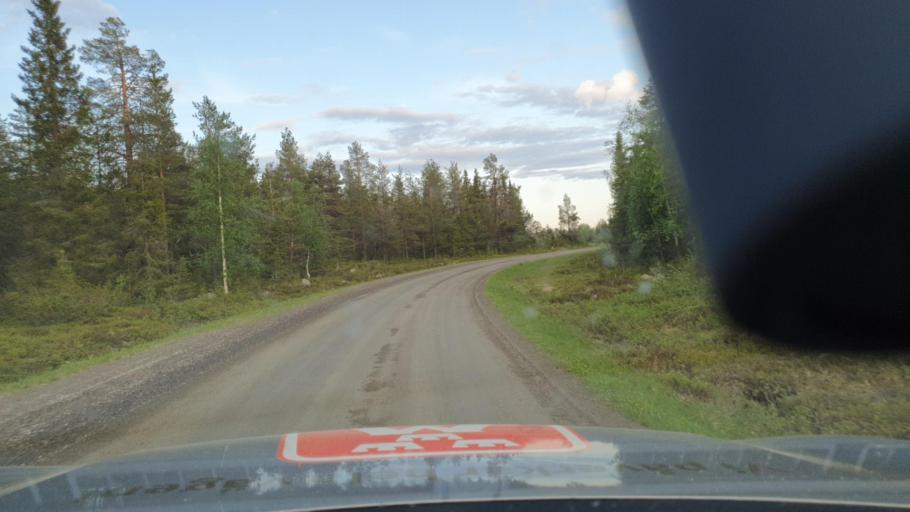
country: SE
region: Norrbotten
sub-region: Bodens Kommun
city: Boden
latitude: 66.5513
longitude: 21.4645
